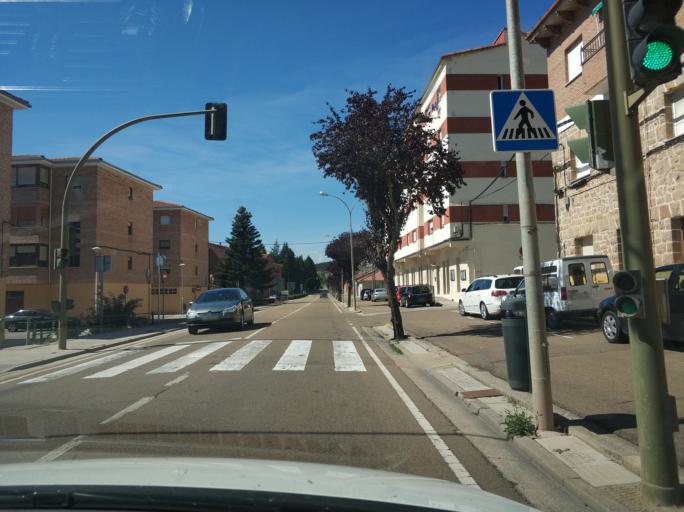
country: ES
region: Castille and Leon
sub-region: Provincia de Palencia
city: Aguilar de Campoo
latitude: 42.7953
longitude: -4.2653
